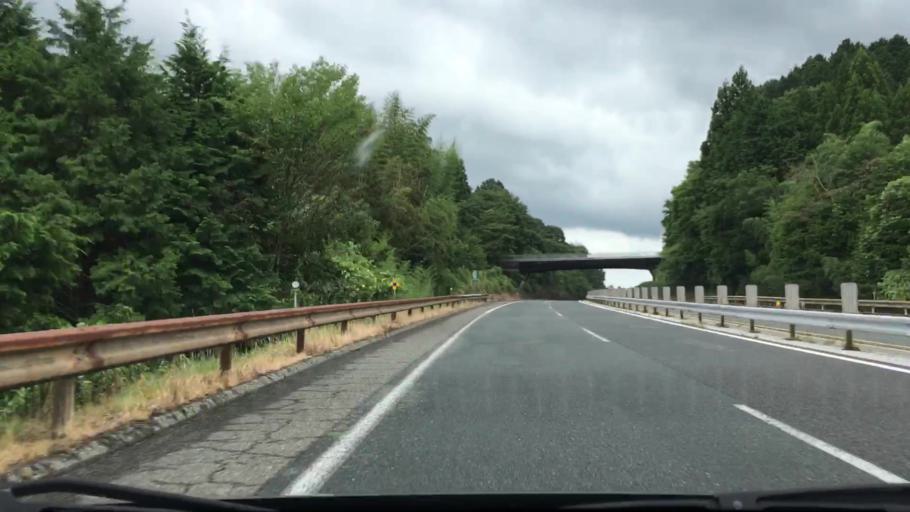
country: JP
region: Okayama
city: Niimi
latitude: 34.9275
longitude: 133.3256
